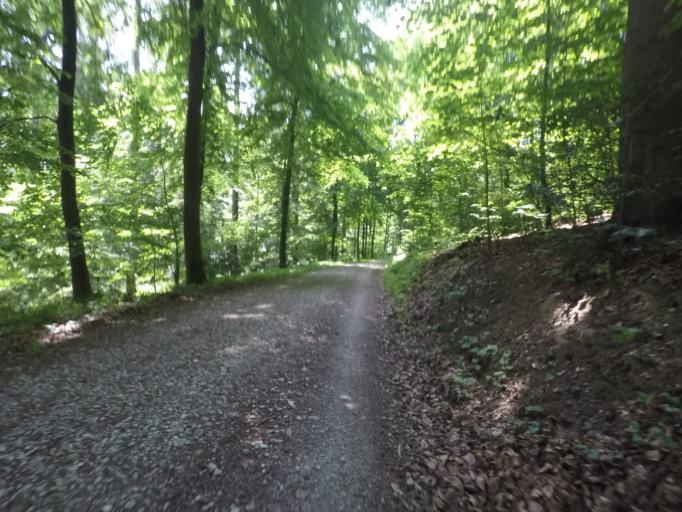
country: DE
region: North Rhine-Westphalia
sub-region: Regierungsbezirk Detmold
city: Bielefeld
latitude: 52.0127
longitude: 8.4961
